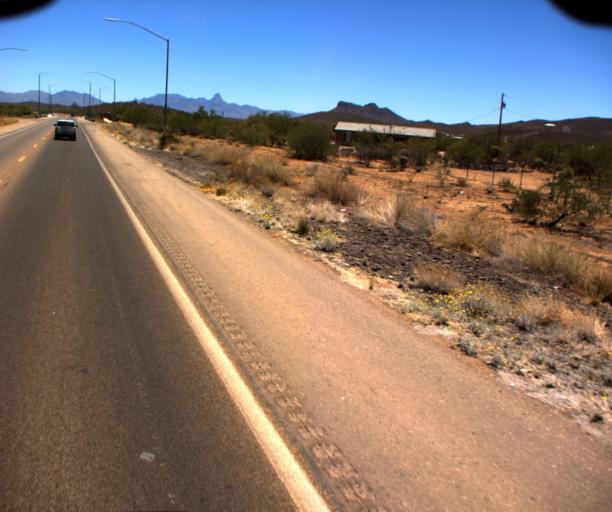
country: US
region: Arizona
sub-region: Pima County
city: Sells
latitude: 31.9200
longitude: -111.8855
